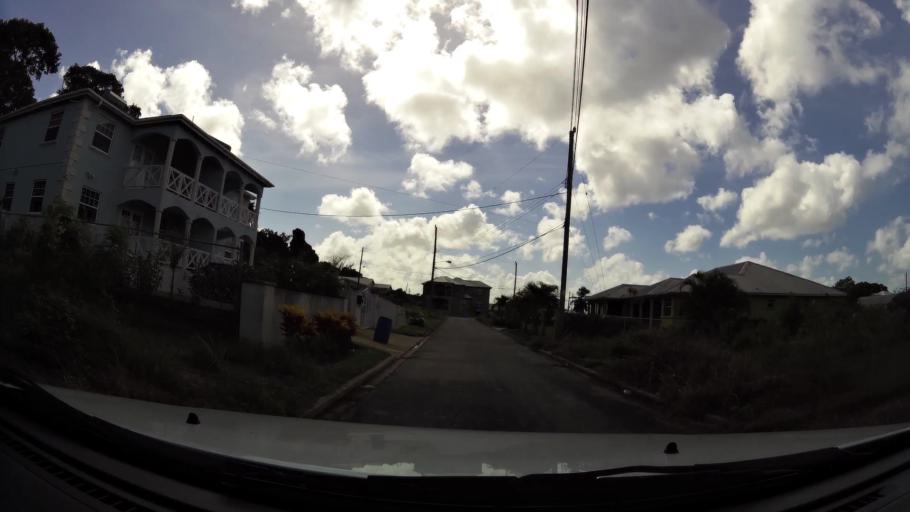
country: BB
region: Saint Lucy
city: Checker Hall
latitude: 13.2724
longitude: -59.6434
